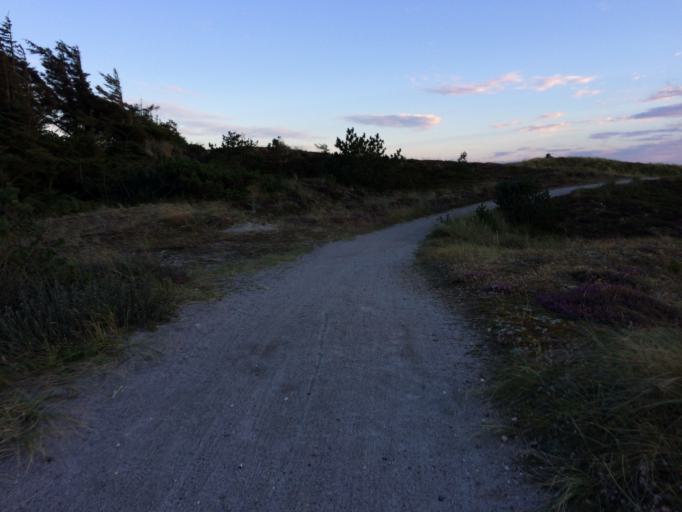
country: DK
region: Central Jutland
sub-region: Ringkobing-Skjern Kommune
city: Hvide Sande
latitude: 55.8740
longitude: 8.1708
